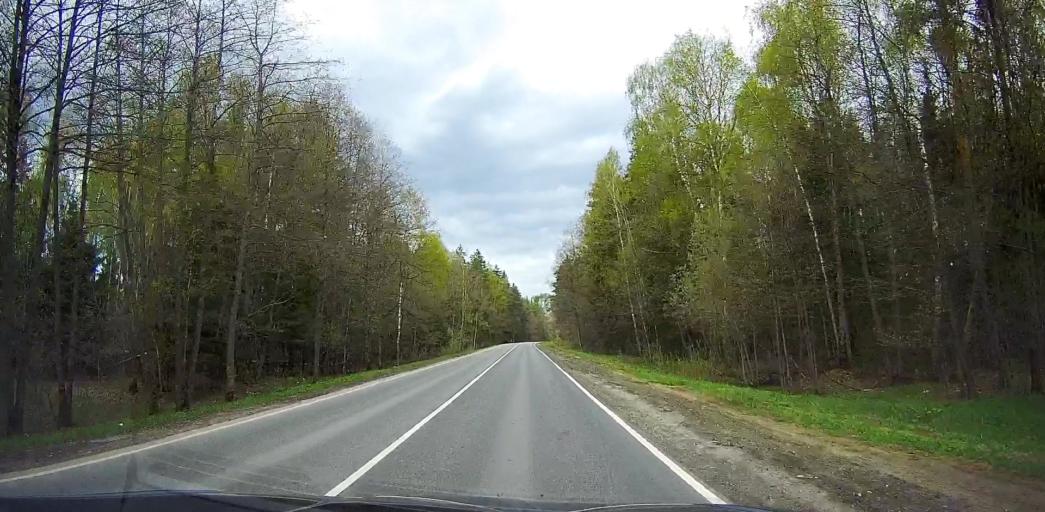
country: RU
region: Moskovskaya
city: Ashitkovo
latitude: 55.4793
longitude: 38.6145
